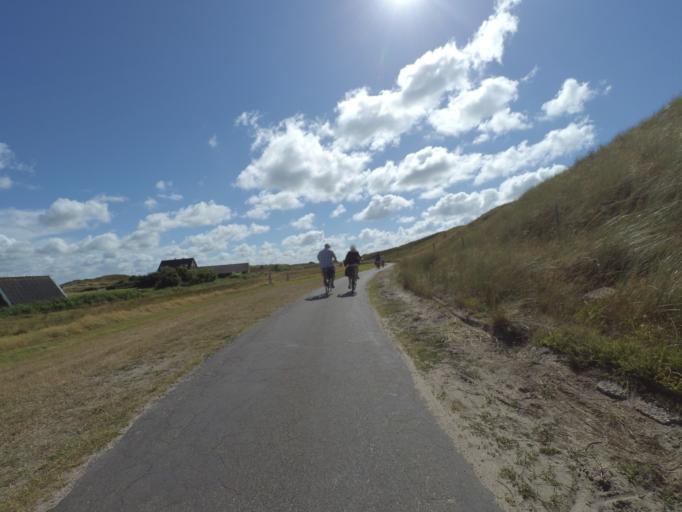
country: NL
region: North Holland
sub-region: Gemeente Texel
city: Den Burg
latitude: 53.1125
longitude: 4.7949
